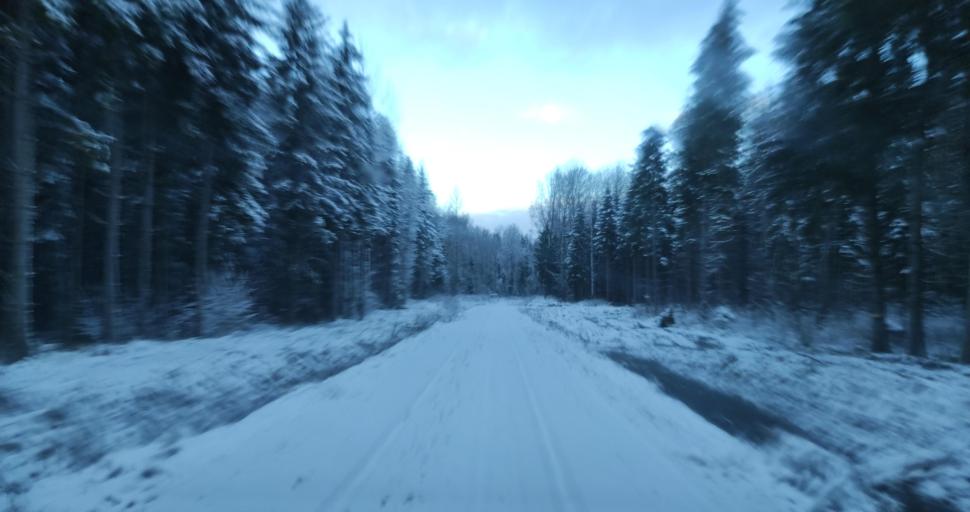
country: LV
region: Skrunda
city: Skrunda
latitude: 56.5827
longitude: 21.9188
